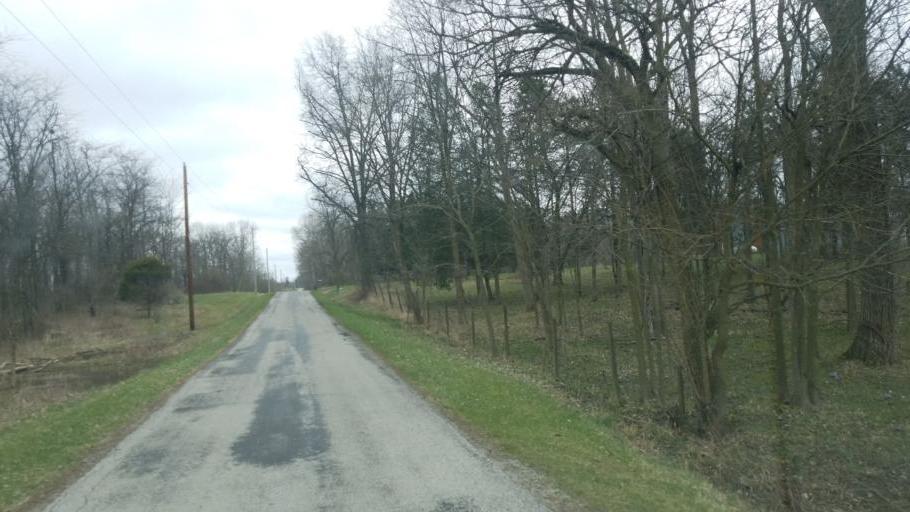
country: US
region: Ohio
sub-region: Hardin County
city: Forest
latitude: 40.6508
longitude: -83.3928
